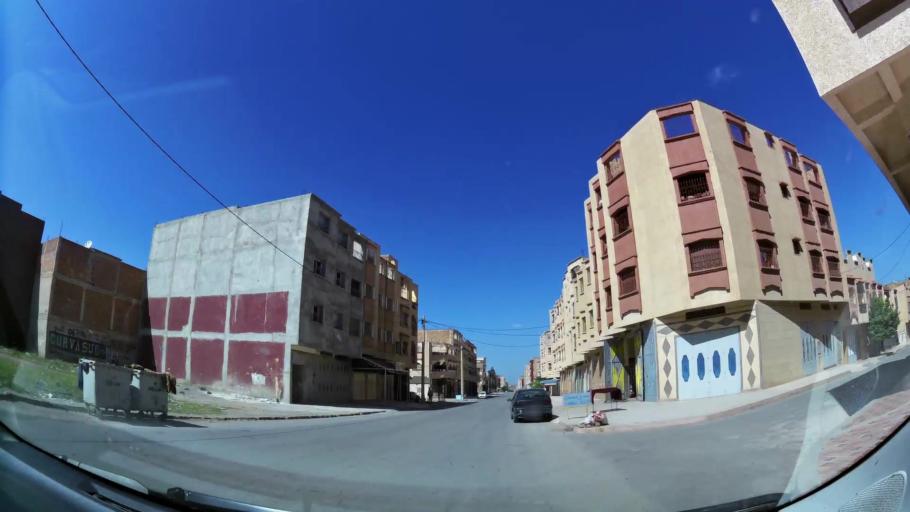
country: MA
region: Oriental
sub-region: Oujda-Angad
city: Oujda
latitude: 34.6850
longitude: -1.9423
